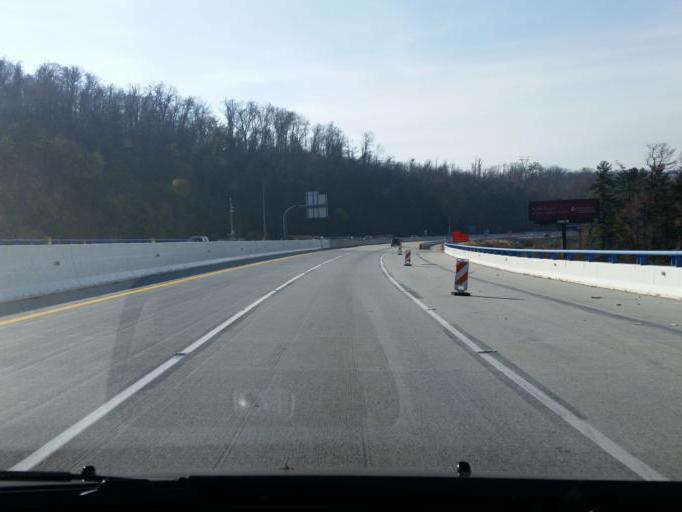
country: US
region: Pennsylvania
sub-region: Dauphin County
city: Highspire
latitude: 40.2003
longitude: -76.8093
